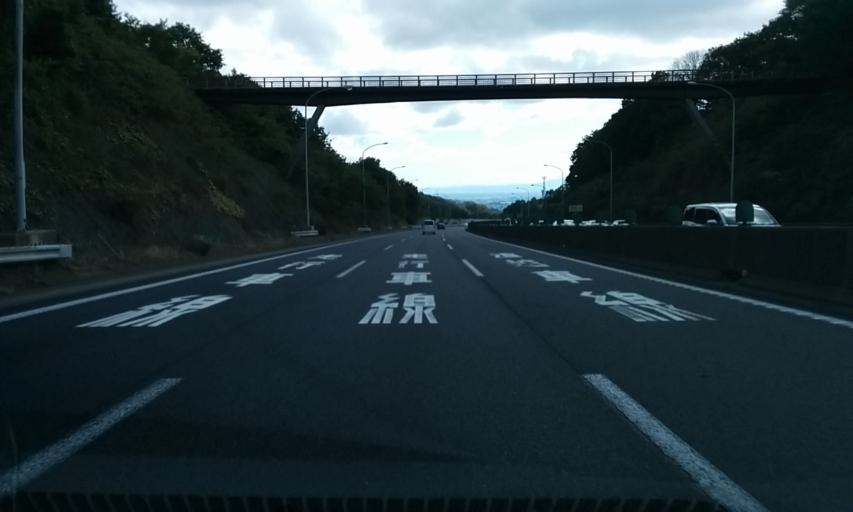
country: JP
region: Hyogo
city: Sandacho
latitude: 34.8354
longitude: 135.2761
